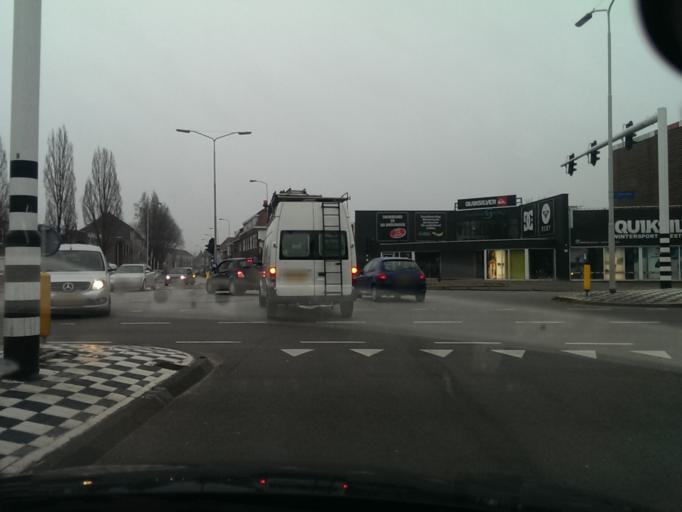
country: NL
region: North Brabant
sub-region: Gemeente Eindhoven
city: Eindhoven
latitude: 51.4359
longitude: 5.4517
